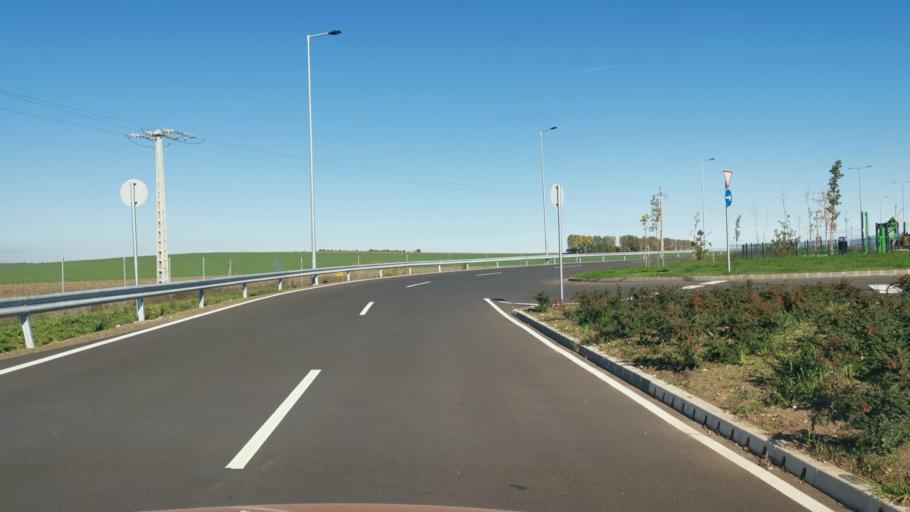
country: HU
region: Borsod-Abauj-Zemplen
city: Halmaj
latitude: 48.2936
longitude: 21.0345
